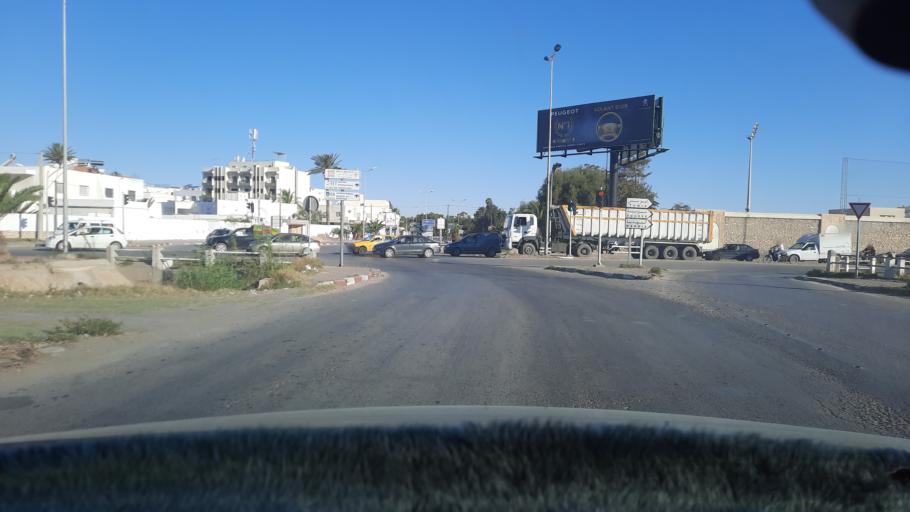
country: TN
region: Safaqis
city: Sfax
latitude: 34.7312
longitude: 10.7466
